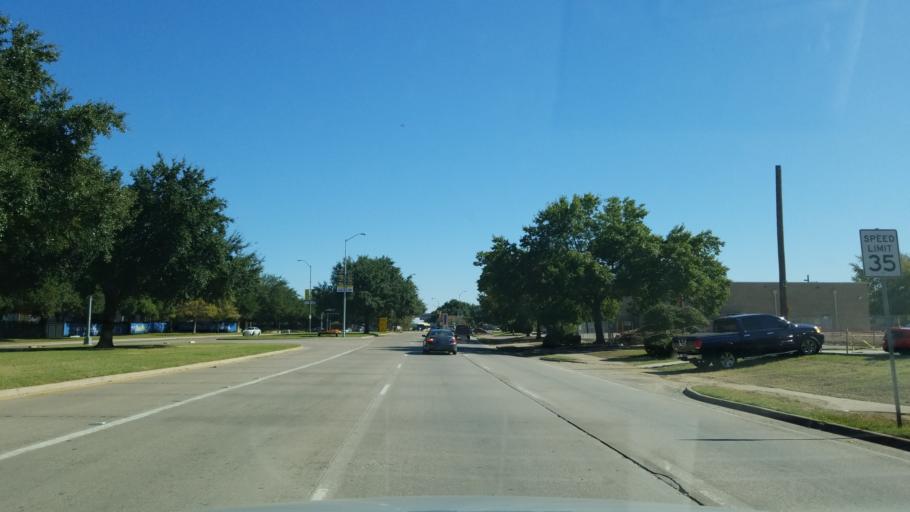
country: US
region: Texas
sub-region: Dallas County
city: Dallas
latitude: 32.7761
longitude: -96.7637
